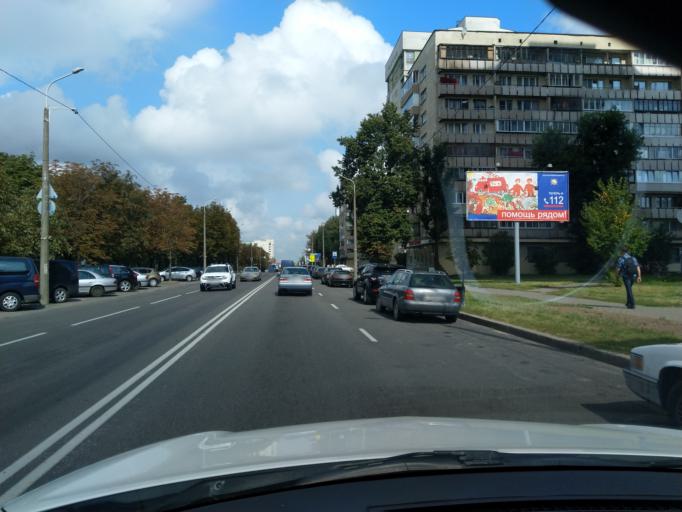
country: BY
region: Minsk
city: Minsk
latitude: 53.8971
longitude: 27.5877
